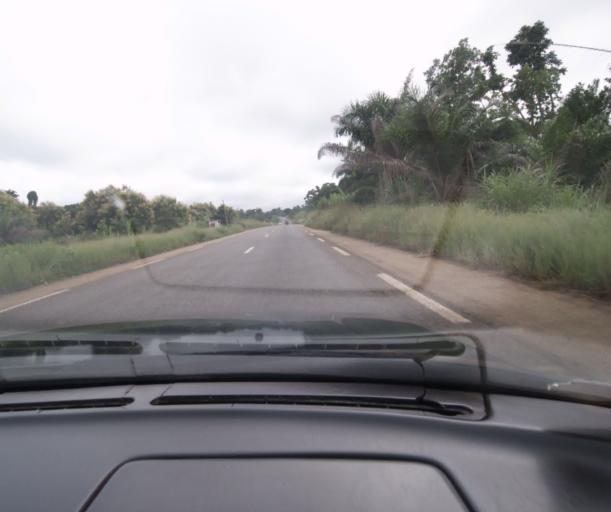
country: CM
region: Centre
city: Ombesa
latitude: 4.5657
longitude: 11.2647
